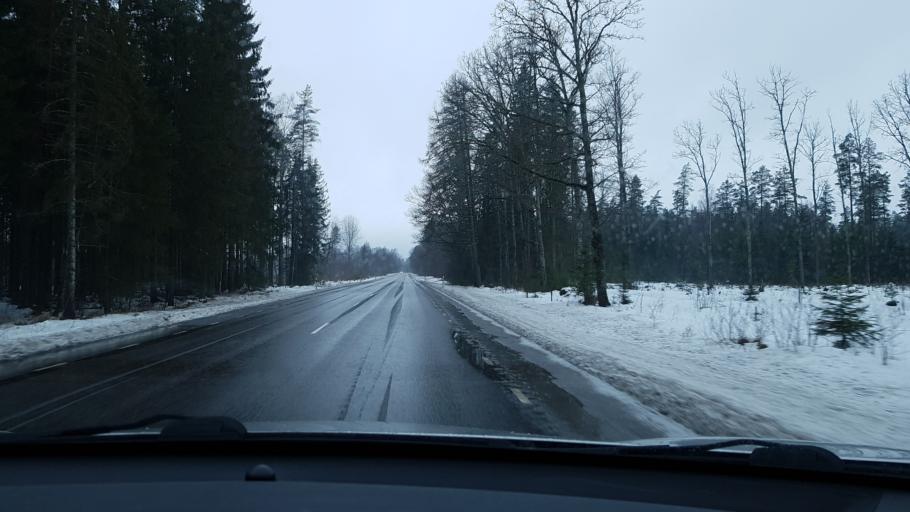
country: EE
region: Paernumaa
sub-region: Vaendra vald (alev)
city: Vandra
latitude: 58.8179
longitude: 25.1594
